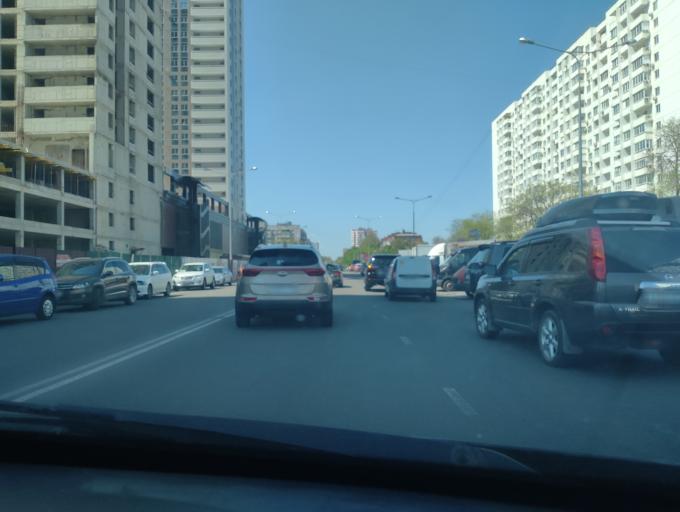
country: RU
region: Krasnodarskiy
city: Krasnodar
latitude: 45.0627
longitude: 39.0105
